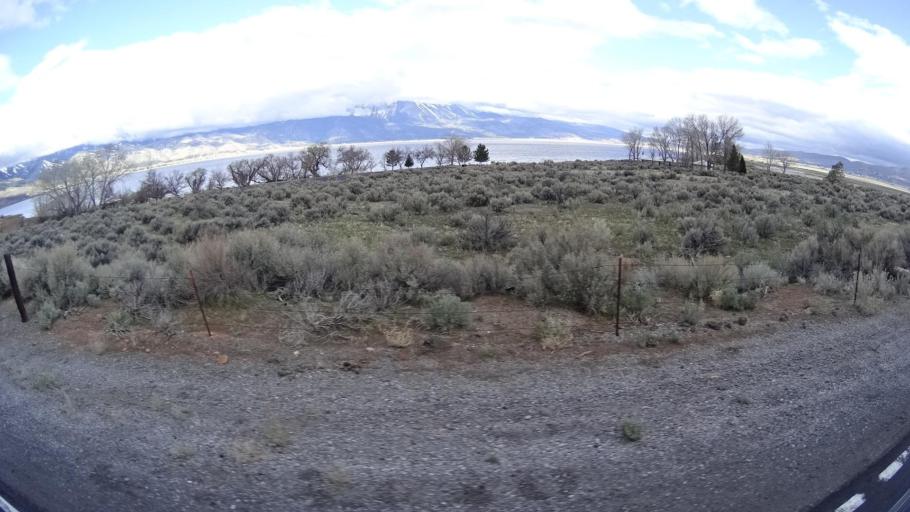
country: US
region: Nevada
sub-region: Carson City
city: Carson City
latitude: 39.2374
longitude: -119.7679
